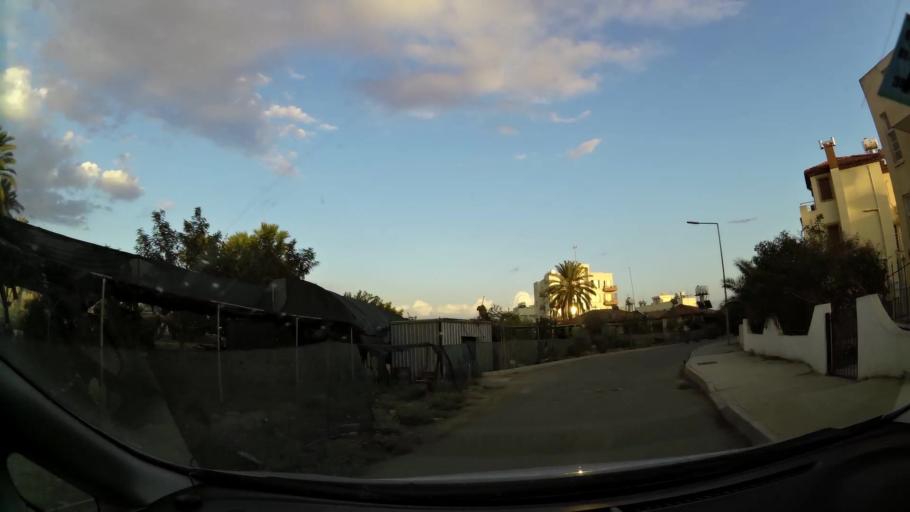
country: CY
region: Lefkosia
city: Nicosia
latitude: 35.1946
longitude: 33.3723
